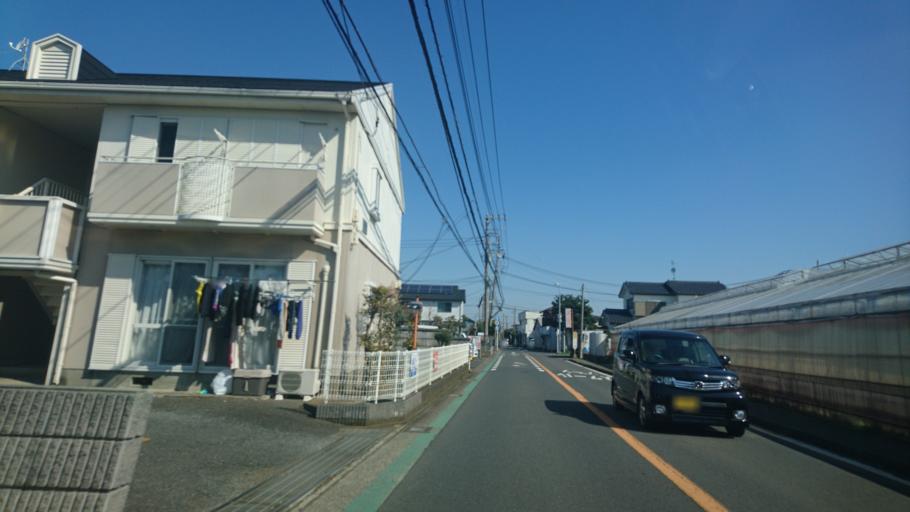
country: JP
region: Kanagawa
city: Fujisawa
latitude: 35.3688
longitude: 139.4829
